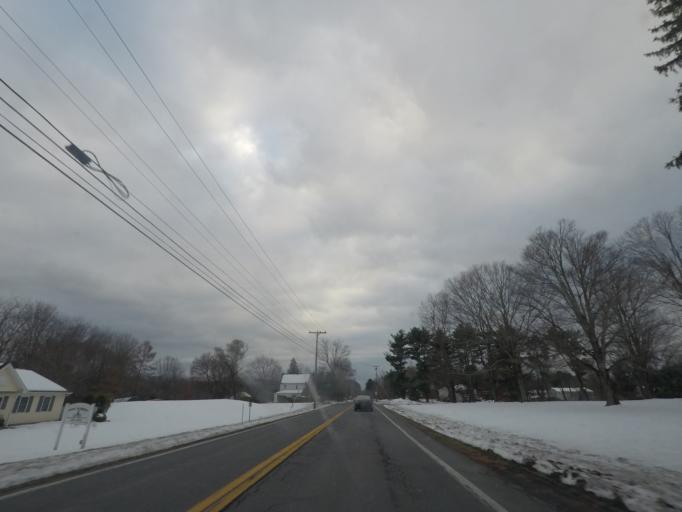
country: US
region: New York
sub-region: Ulster County
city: New Paltz
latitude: 41.7155
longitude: -74.0849
